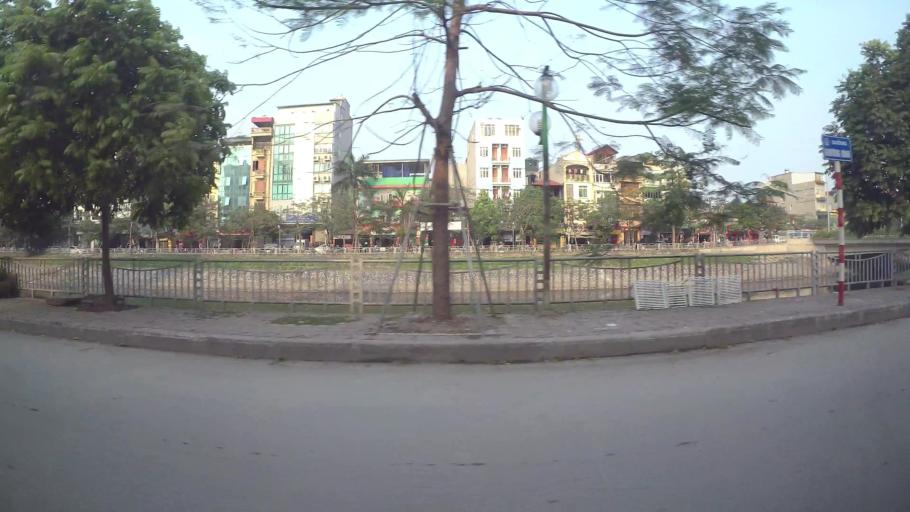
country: VN
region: Ha Noi
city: Thanh Xuan
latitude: 20.9868
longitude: 105.8132
